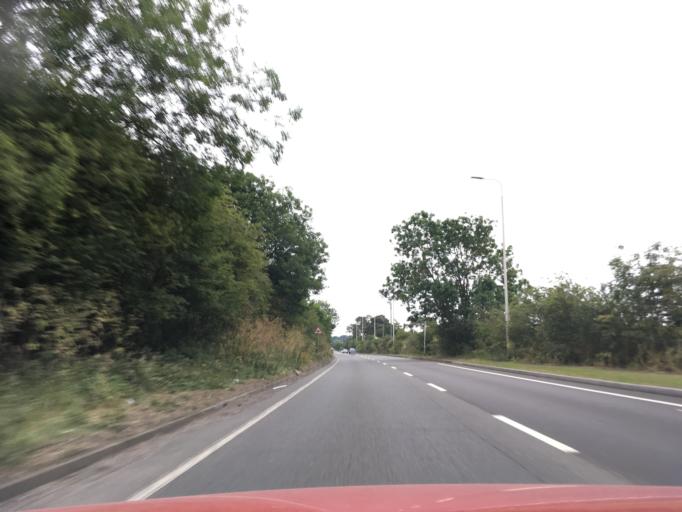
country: GB
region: England
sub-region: Hertfordshire
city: Flamstead
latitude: 51.8302
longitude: -0.4481
